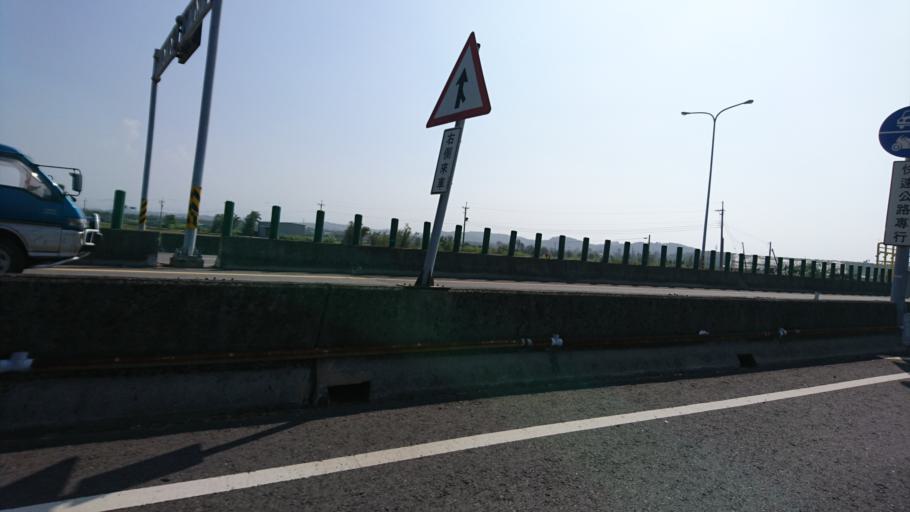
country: TW
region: Taiwan
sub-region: Miaoli
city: Miaoli
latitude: 24.6768
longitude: 120.8425
